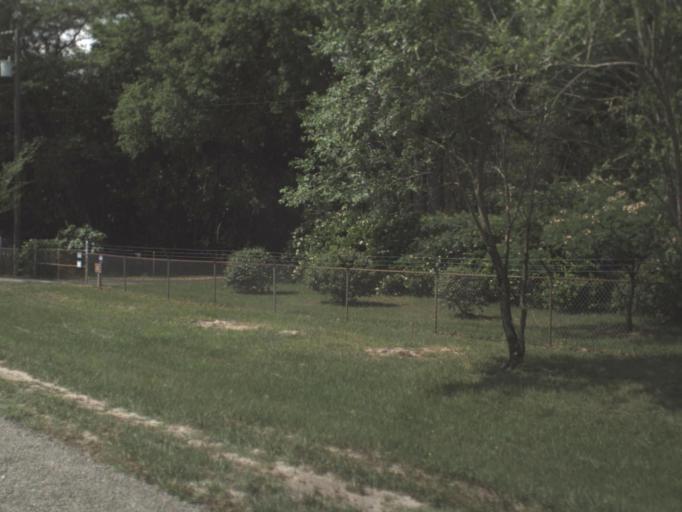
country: US
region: Florida
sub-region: Saint Johns County
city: Butler Beach
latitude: 29.6774
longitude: -81.2923
